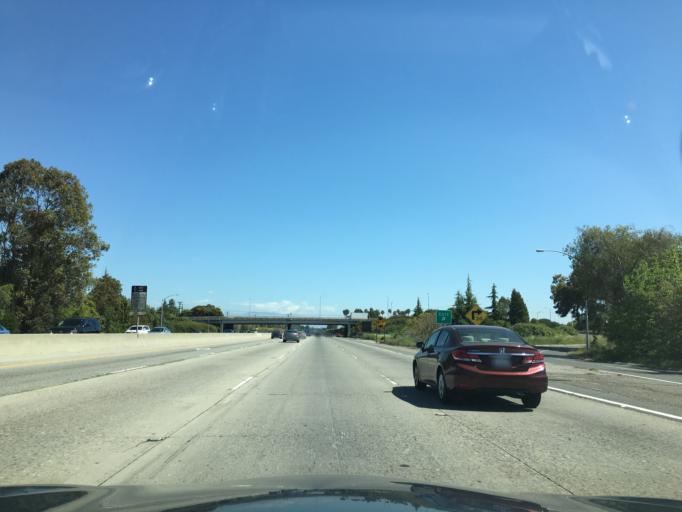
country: US
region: California
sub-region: Santa Clara County
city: Sunnyvale
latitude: 37.3995
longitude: -122.0306
